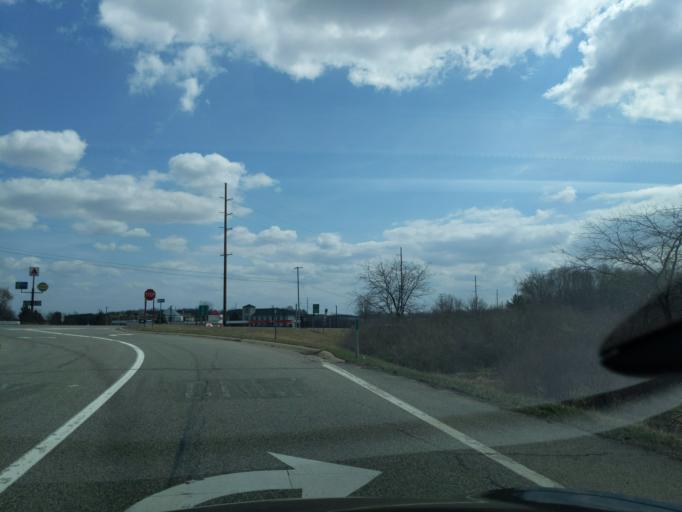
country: US
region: Michigan
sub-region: Calhoun County
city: Marshall
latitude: 42.2935
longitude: -84.9652
